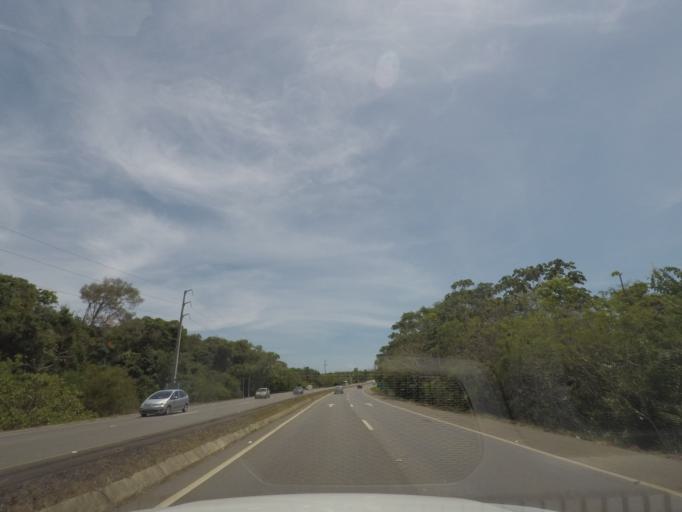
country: BR
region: Bahia
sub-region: Mata De Sao Joao
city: Mata de Sao Joao
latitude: -12.5829
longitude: -38.0408
